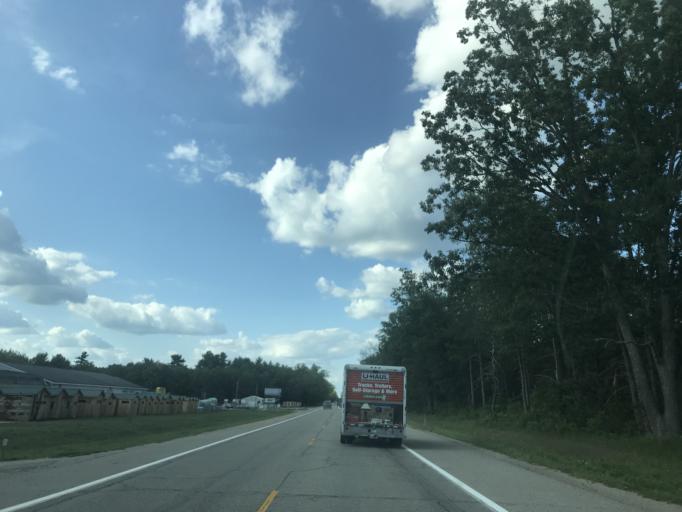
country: US
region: Michigan
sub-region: Newaygo County
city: White Cloud
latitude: 43.4869
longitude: -85.7733
